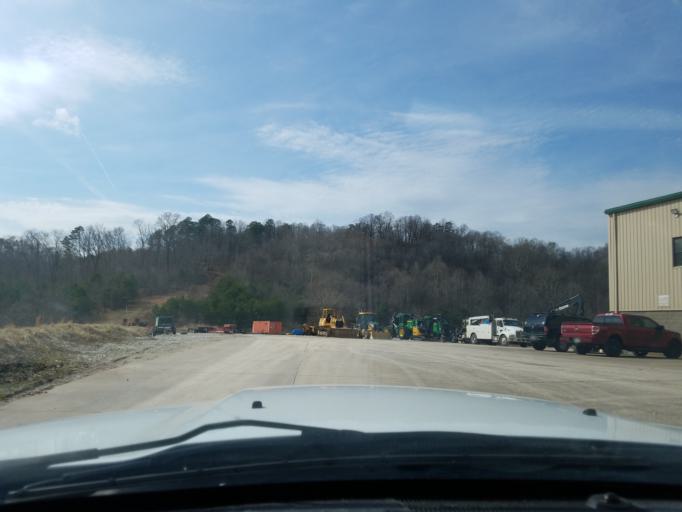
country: US
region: West Virginia
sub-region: Kanawha County
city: Cross Lanes
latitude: 38.4076
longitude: -81.7983
